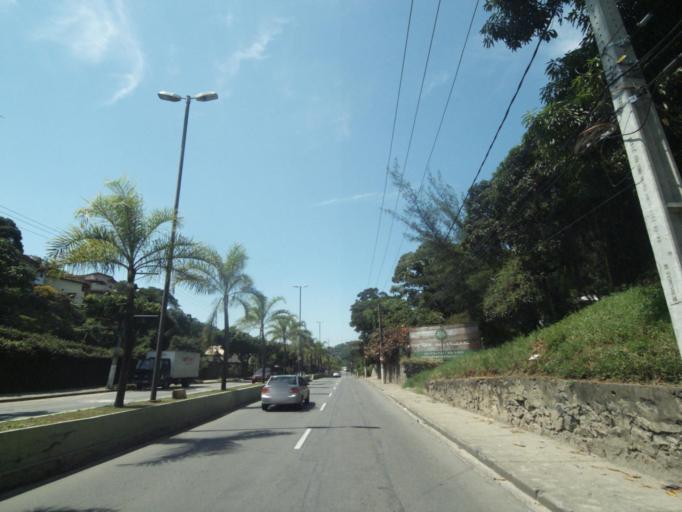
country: BR
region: Rio de Janeiro
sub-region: Niteroi
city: Niteroi
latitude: -22.9033
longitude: -43.0463
